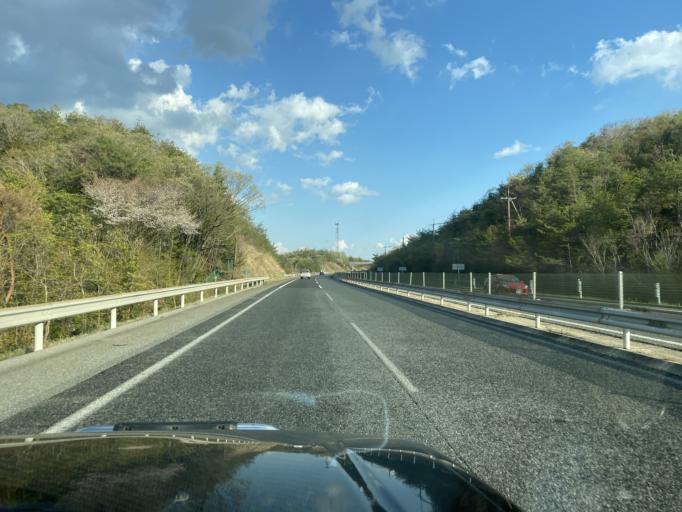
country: JP
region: Hyogo
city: Sandacho
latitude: 34.9558
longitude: 135.1355
